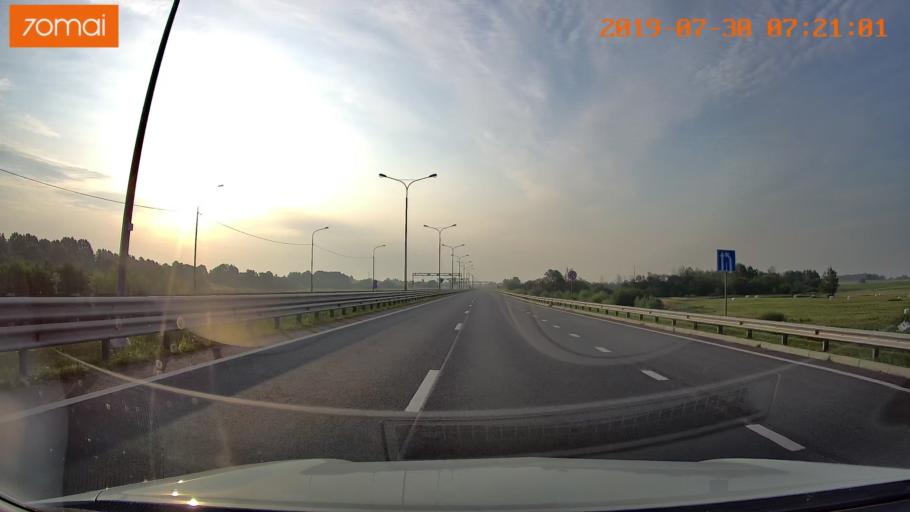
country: RU
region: Kaliningrad
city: Bol'shoe Isakovo
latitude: 54.6983
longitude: 20.7175
